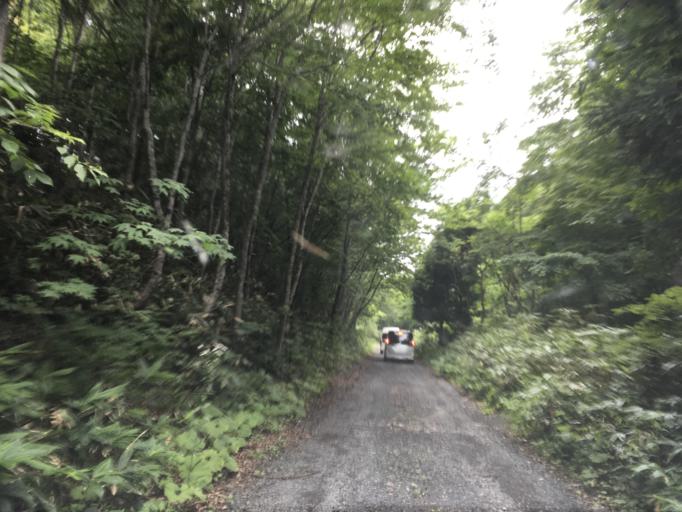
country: JP
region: Iwate
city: Ichinoseki
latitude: 38.9497
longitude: 140.8568
